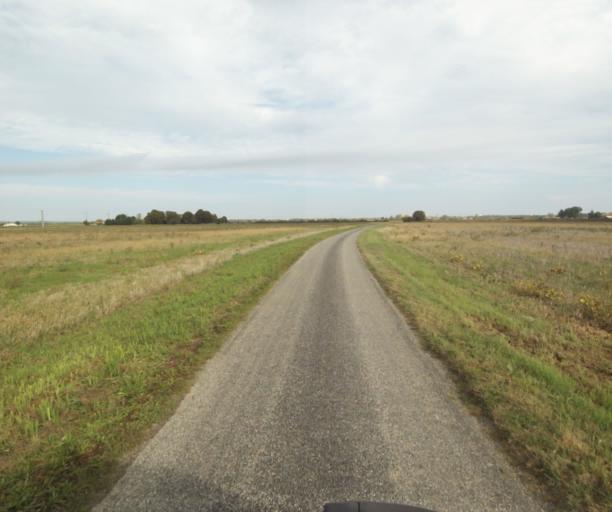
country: FR
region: Midi-Pyrenees
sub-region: Departement du Tarn-et-Garonne
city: Finhan
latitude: 43.9273
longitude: 1.2247
